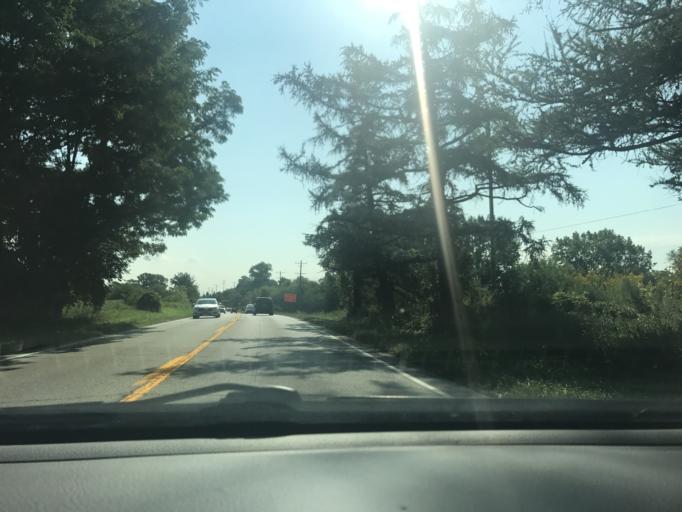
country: US
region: Illinois
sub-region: Kane County
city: Pingree Grove
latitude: 42.0449
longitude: -88.3824
